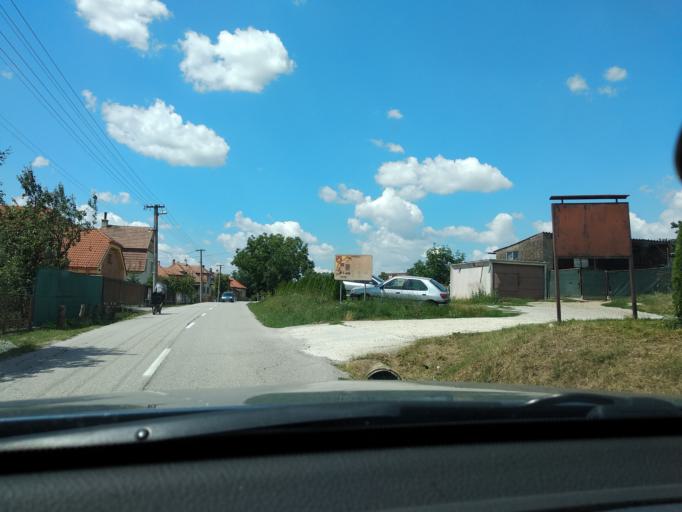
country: SK
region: Nitriansky
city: Banovce nad Bebravou
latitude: 48.6969
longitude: 18.2017
